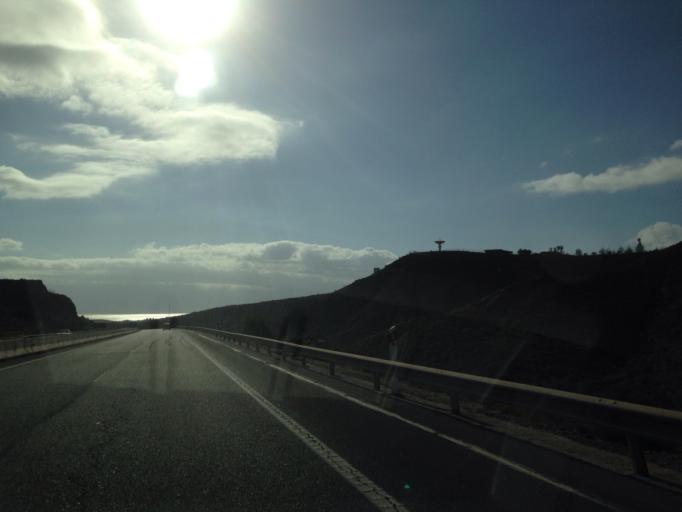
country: ES
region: Canary Islands
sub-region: Provincia de Las Palmas
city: Maspalomas
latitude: 27.7684
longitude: -15.6330
